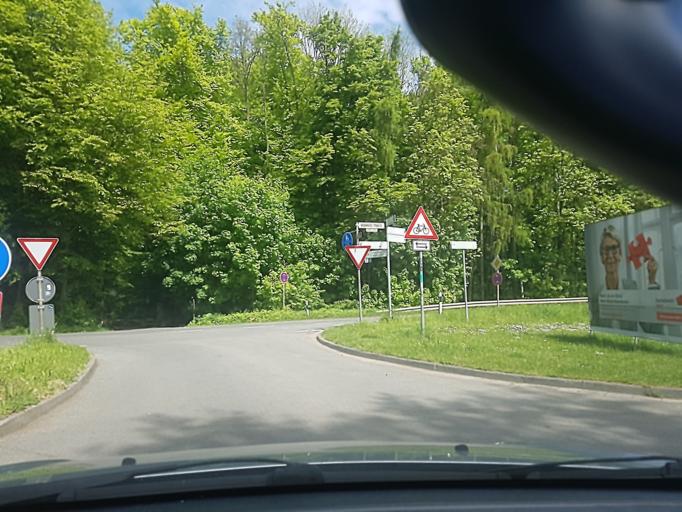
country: DE
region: Hesse
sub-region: Regierungsbezirk Darmstadt
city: Darmstadt
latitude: 49.8909
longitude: 8.6973
